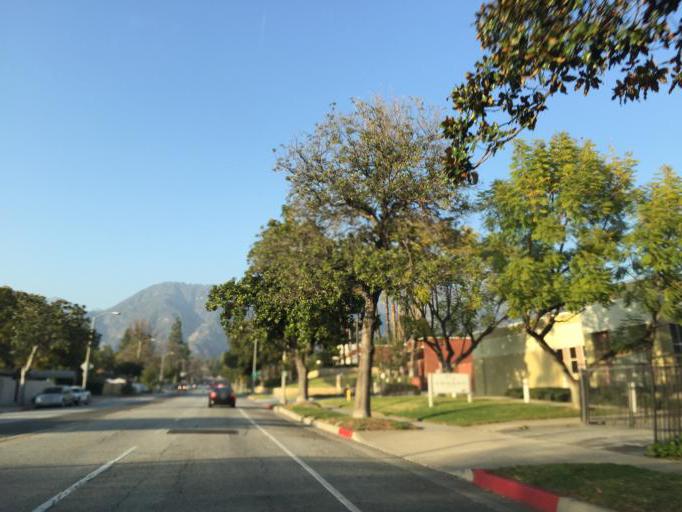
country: US
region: California
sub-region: Los Angeles County
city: East Pasadena
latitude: 34.1554
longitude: -118.0818
